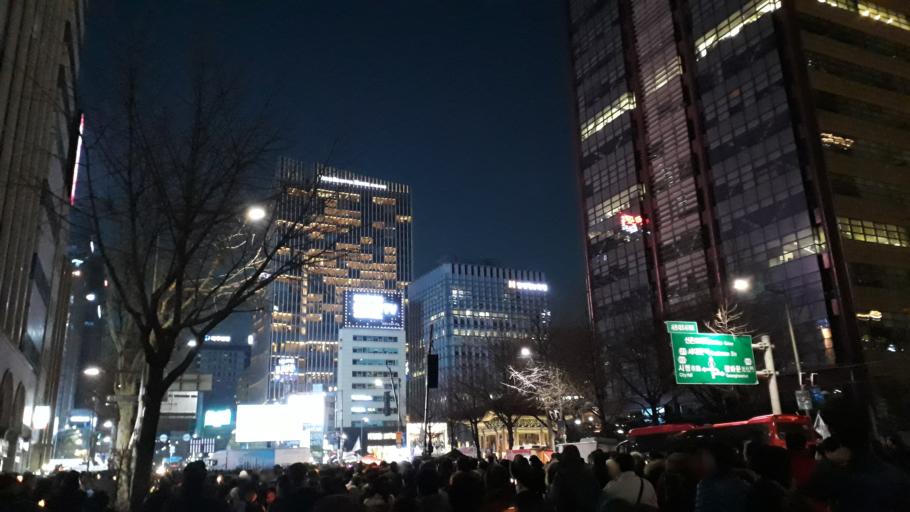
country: KR
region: Seoul
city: Seoul
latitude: 37.5697
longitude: 126.9819
